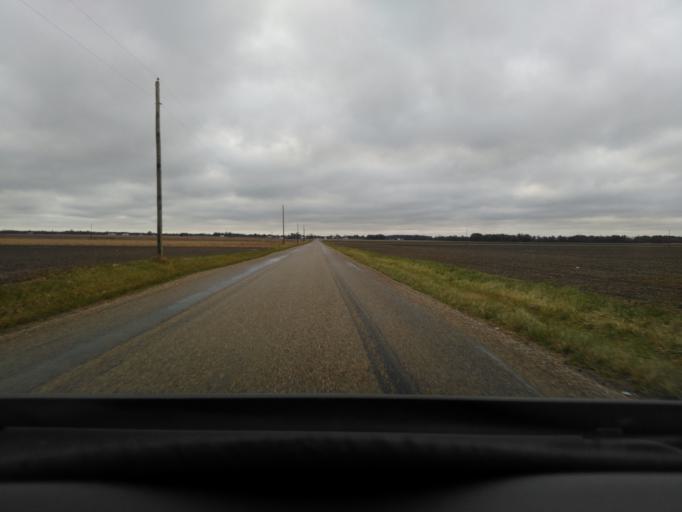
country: US
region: Illinois
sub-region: Effingham County
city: Altamont
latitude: 38.9543
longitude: -88.6635
